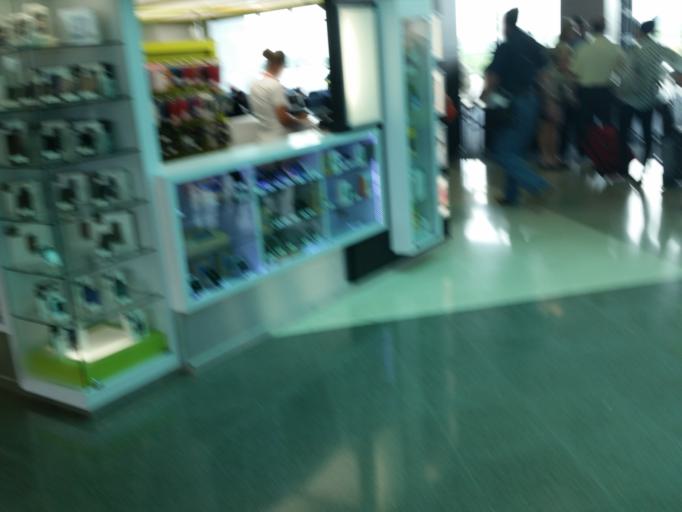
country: PA
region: Panama
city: Tocumen
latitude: 9.0707
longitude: -79.3856
